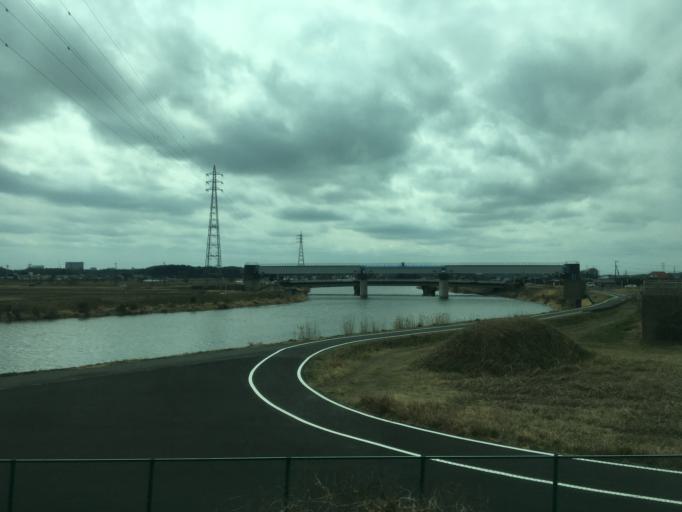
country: JP
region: Ibaraki
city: Ryugasaki
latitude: 35.8428
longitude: 140.1378
